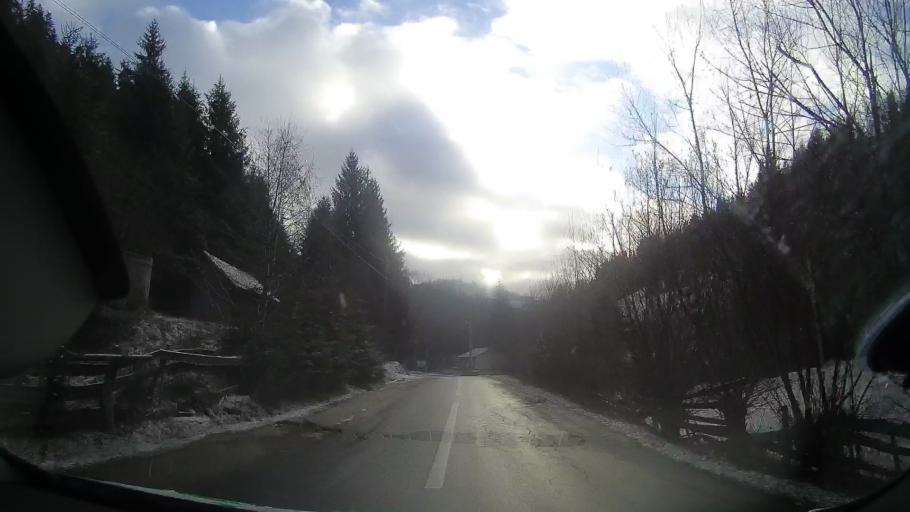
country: RO
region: Alba
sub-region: Comuna Horea
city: Horea
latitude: 46.4965
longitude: 22.9574
